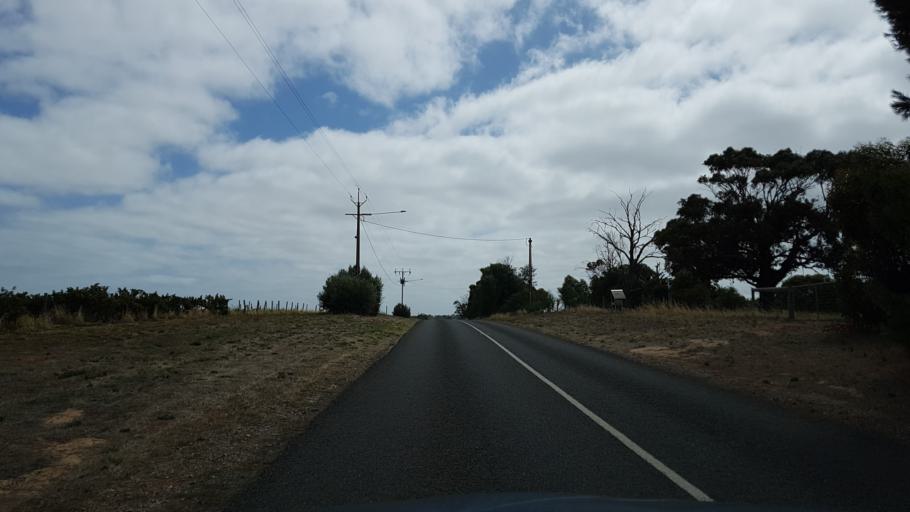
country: AU
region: South Australia
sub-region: Onkaparinga
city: McLaren Vale
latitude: -35.2153
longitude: 138.5177
